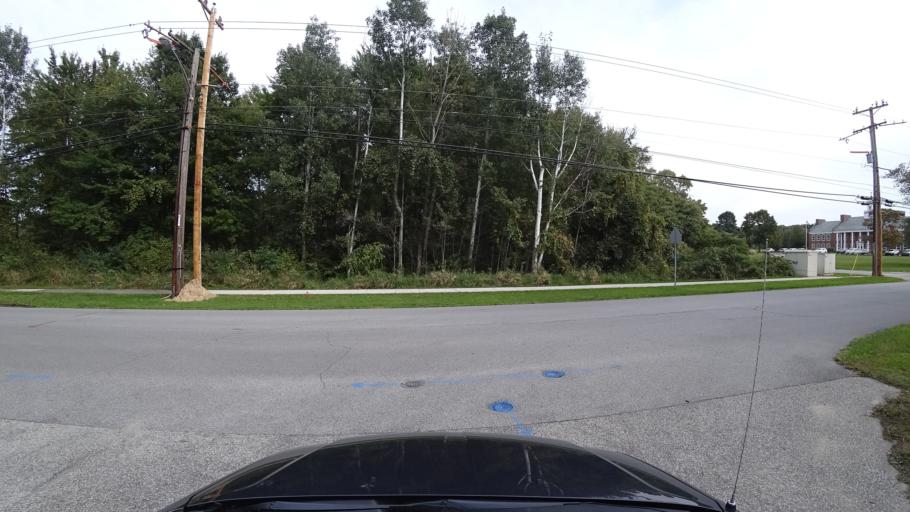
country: US
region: Indiana
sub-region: LaPorte County
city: Long Beach
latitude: 41.7452
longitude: -86.8365
